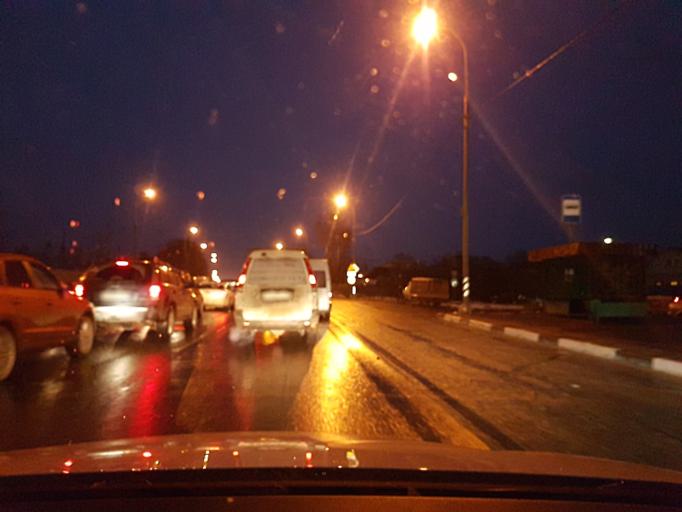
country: RU
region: Moskovskaya
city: Sheremet'yevskiy
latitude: 55.9836
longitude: 37.5286
